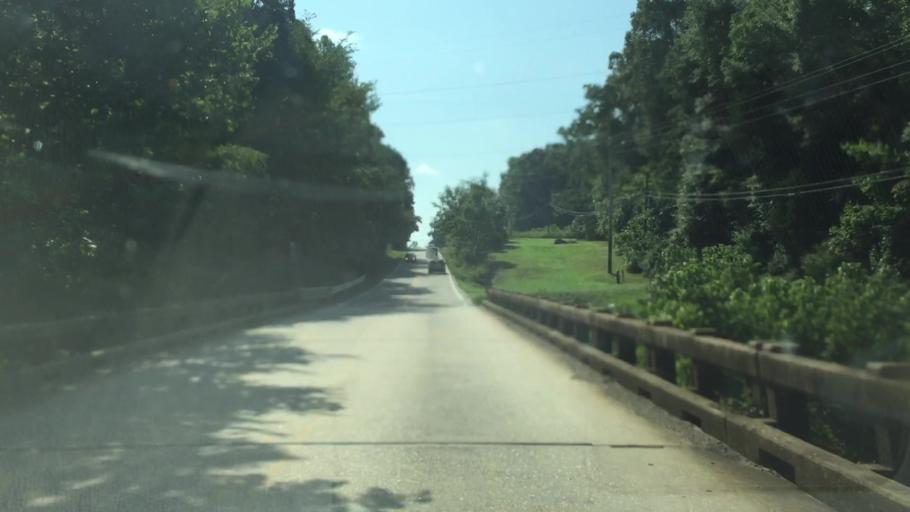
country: US
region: North Carolina
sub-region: Union County
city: Fairview
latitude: 35.1332
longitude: -80.4897
